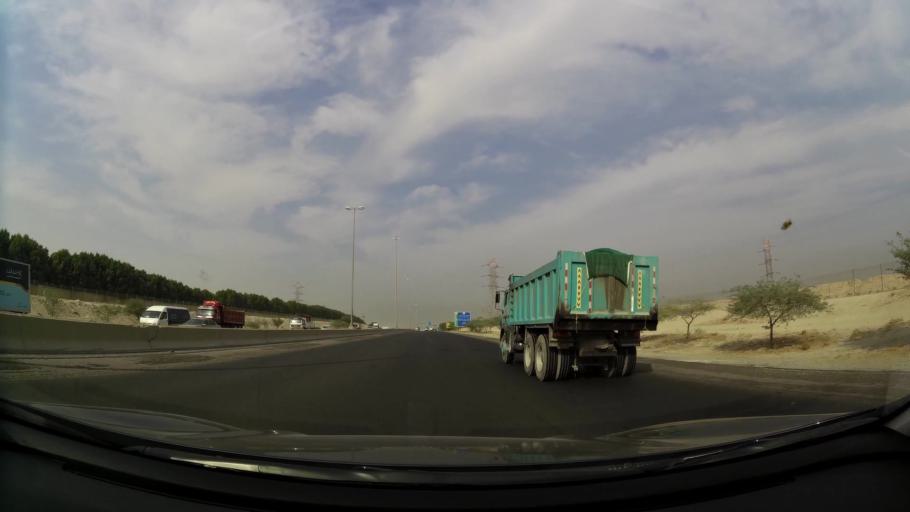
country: KW
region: Muhafazat al Jahra'
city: Al Jahra'
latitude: 29.2926
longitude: 47.7522
